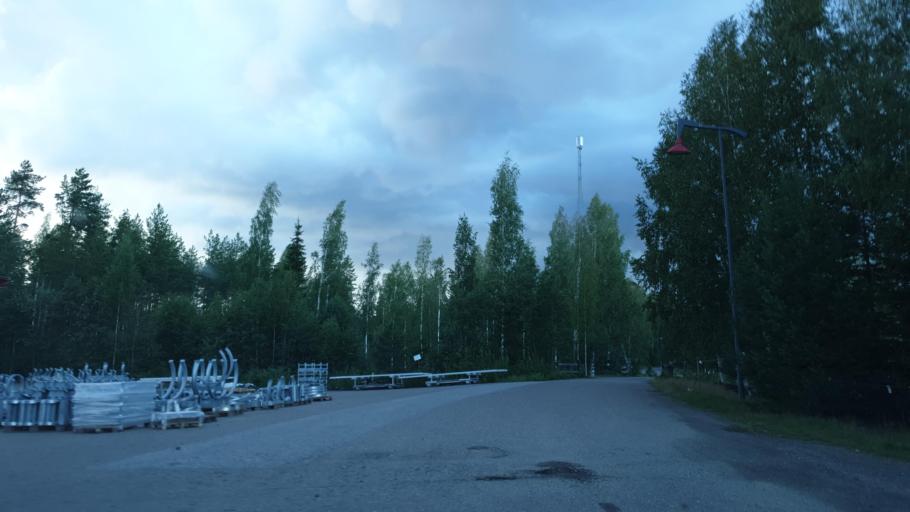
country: FI
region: Northern Savo
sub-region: Varkaus
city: Leppaevirta
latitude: 62.5809
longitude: 27.6074
